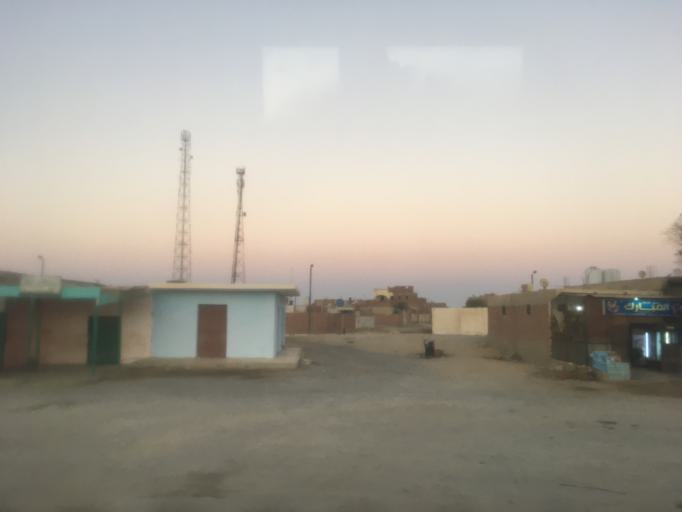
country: EG
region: Red Sea
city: Al Qusayr
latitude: 26.2643
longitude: 34.1959
